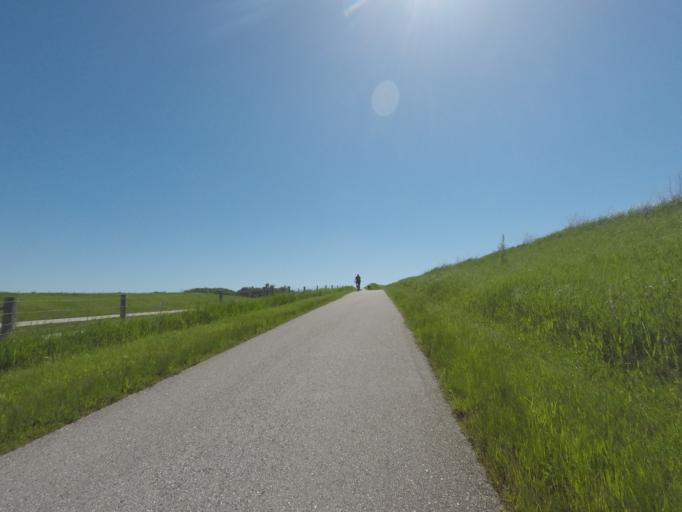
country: US
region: Wisconsin
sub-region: Sheboygan County
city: Sheboygan Falls
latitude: 43.7504
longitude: -87.8376
